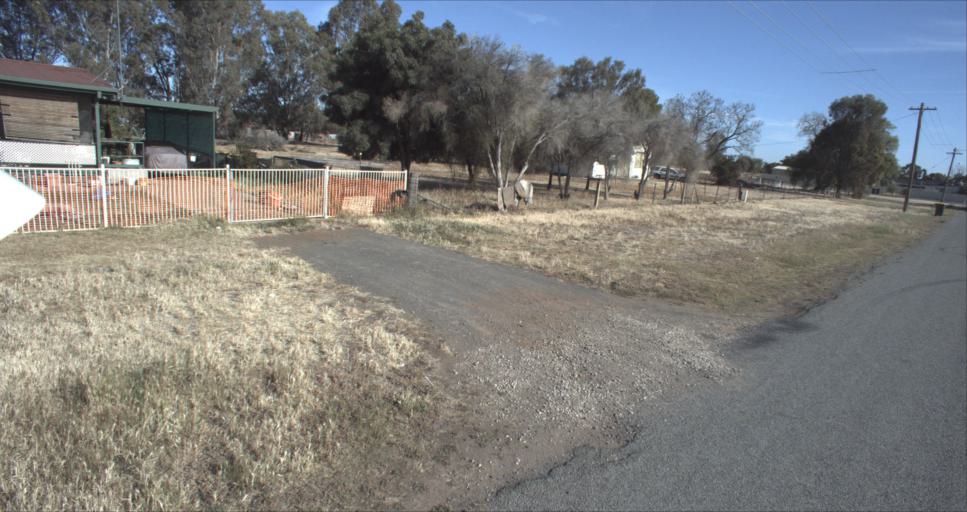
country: AU
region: New South Wales
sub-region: Leeton
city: Leeton
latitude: -34.5949
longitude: 146.4084
